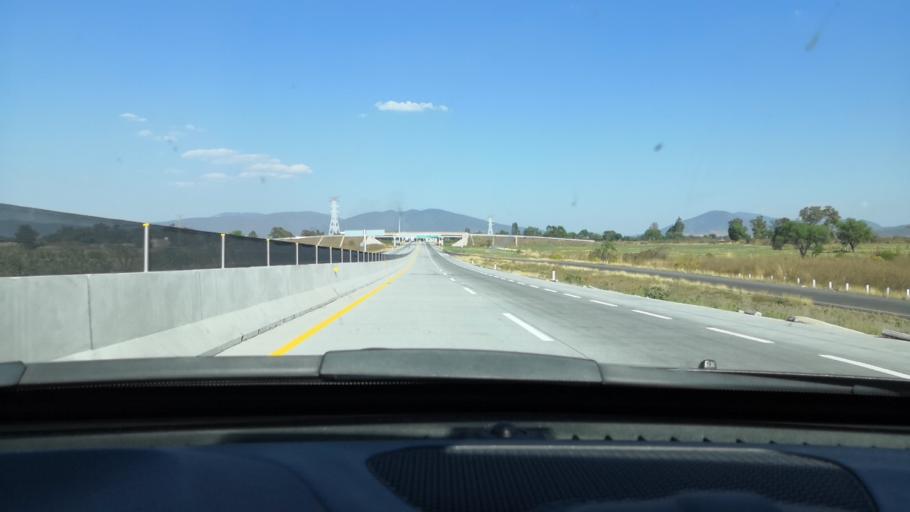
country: MX
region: Jalisco
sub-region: Ixtlahuacan de los Membrillos
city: Los Cedros
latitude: 20.4080
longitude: -103.2276
